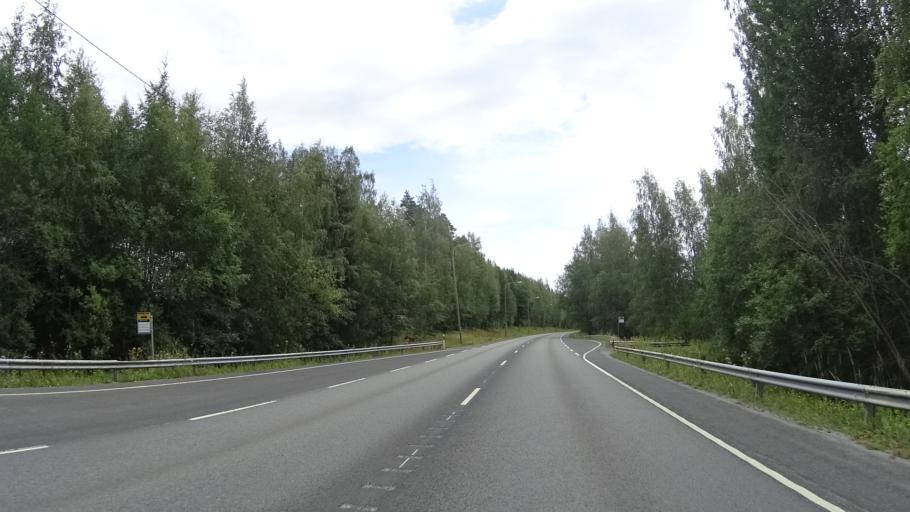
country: FI
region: Pirkanmaa
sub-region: Tampere
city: Kangasala
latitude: 61.4384
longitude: 24.1234
